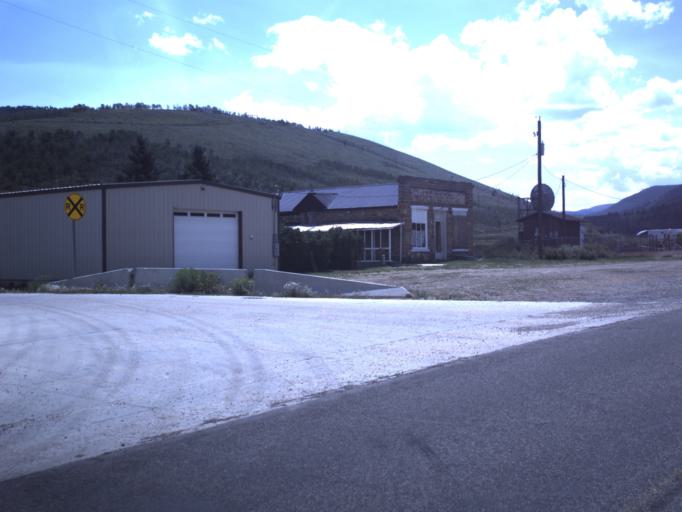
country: US
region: Utah
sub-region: Sanpete County
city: Fairview
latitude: 39.7245
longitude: -111.1609
